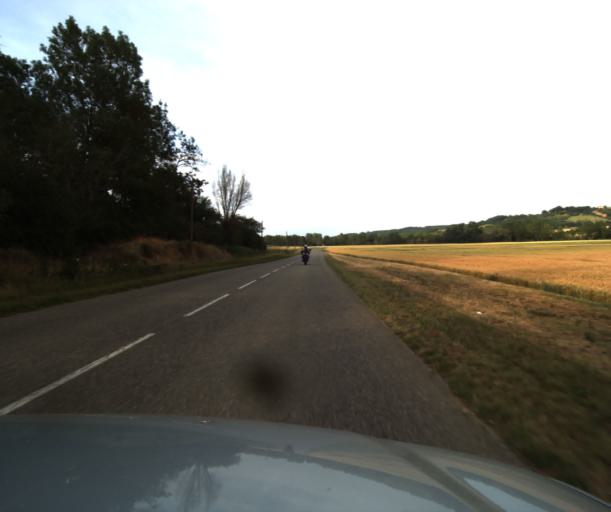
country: FR
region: Midi-Pyrenees
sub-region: Departement du Tarn-et-Garonne
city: Castelsarrasin
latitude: 43.9405
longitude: 1.0921
